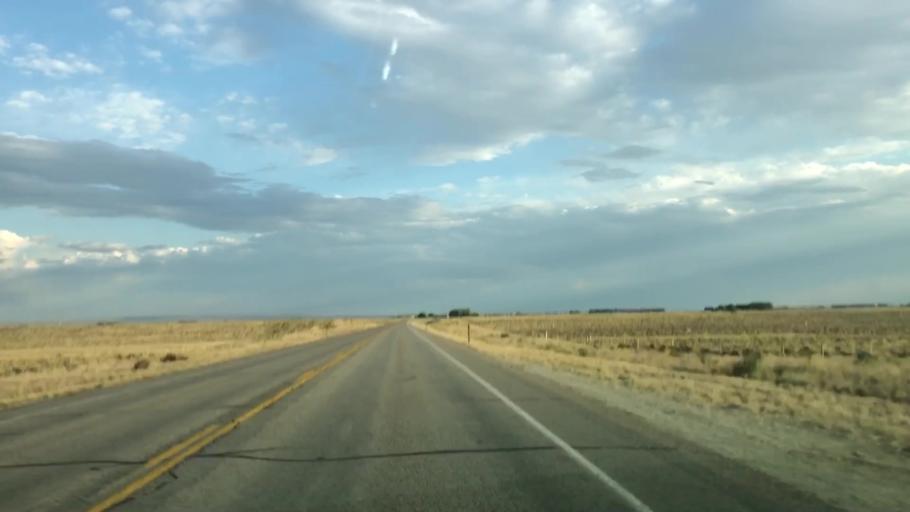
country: US
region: Wyoming
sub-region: Sweetwater County
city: North Rock Springs
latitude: 42.0941
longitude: -109.4428
